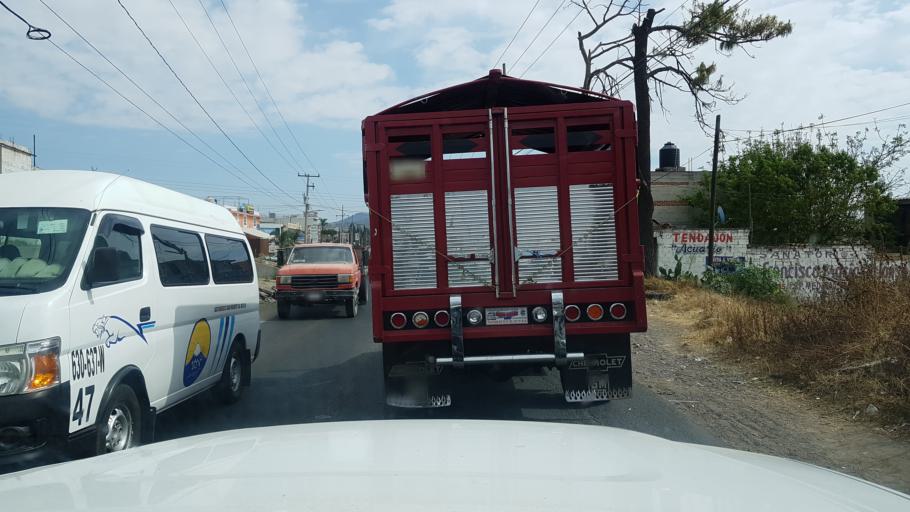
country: MX
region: Tlaxcala
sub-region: Ixtacuixtla de Mariano Matamoros
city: Villa Mariano Matamoros
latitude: 19.2961
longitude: -98.3995
